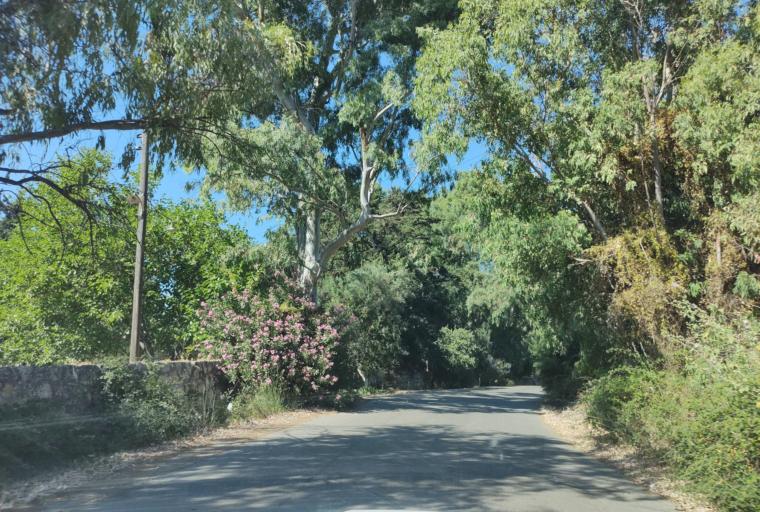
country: GR
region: Crete
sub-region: Nomos Chanias
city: Georgioupolis
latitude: 35.3613
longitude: 24.2525
